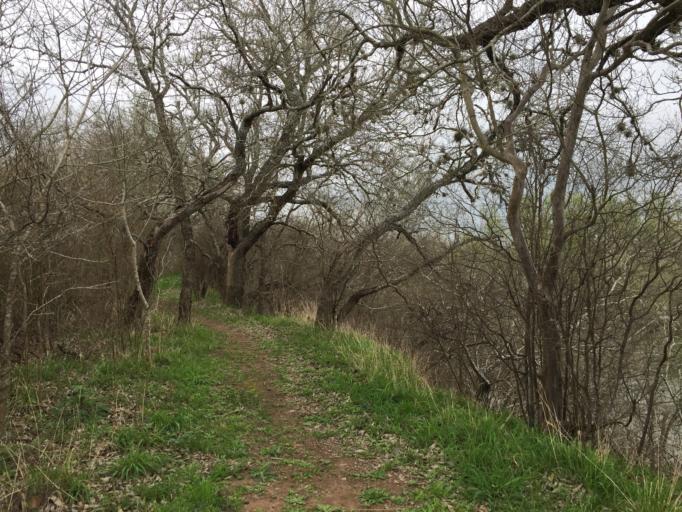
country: US
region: Texas
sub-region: Bastrop County
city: Bastrop
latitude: 30.0820
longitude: -97.3264
